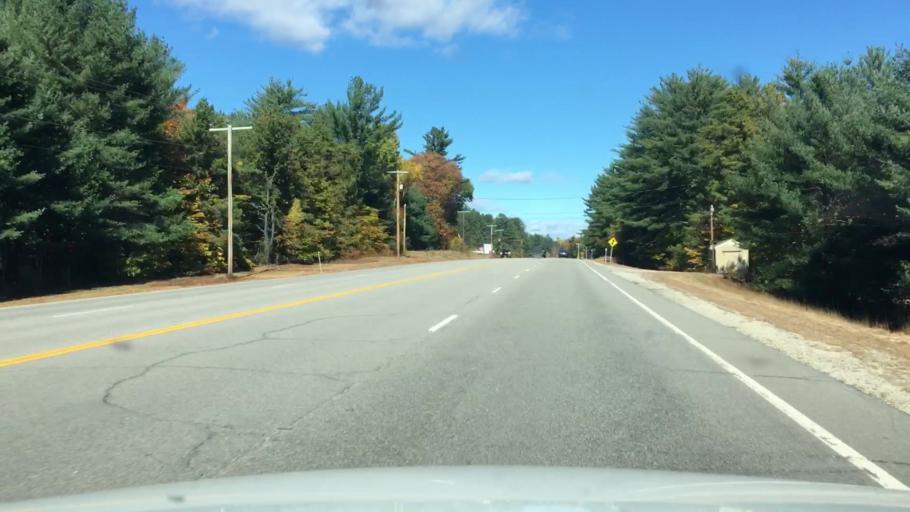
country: US
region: New Hampshire
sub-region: Carroll County
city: Tamworth
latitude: 43.8526
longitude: -71.2059
